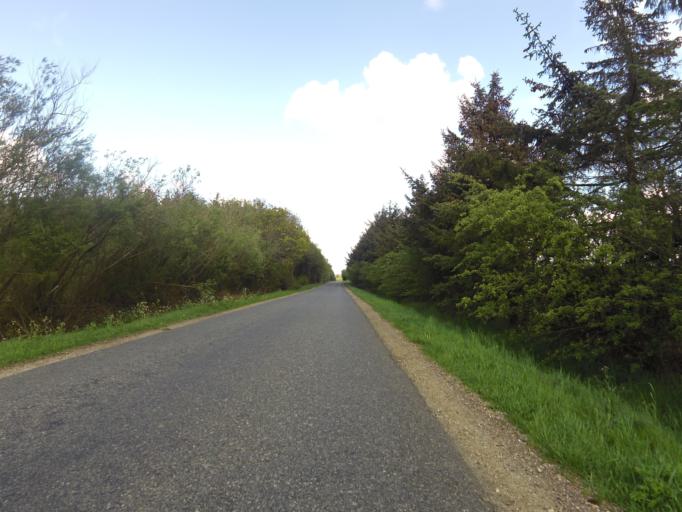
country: DK
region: South Denmark
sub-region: Esbjerg Kommune
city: Ribe
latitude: 55.2632
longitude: 8.7343
